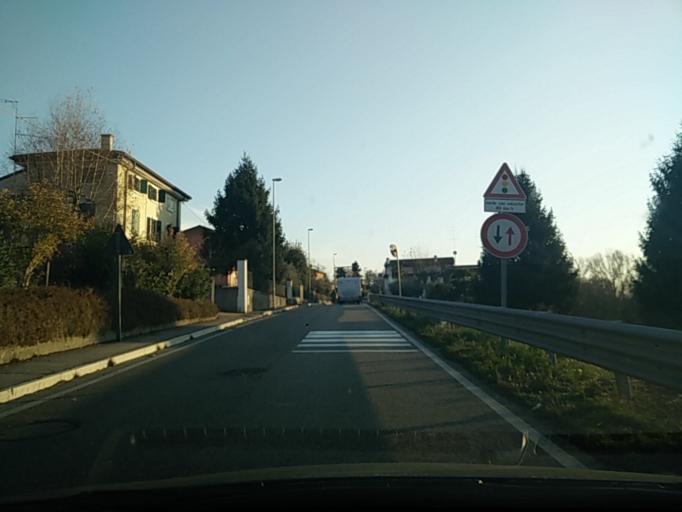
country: IT
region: Veneto
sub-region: Provincia di Verona
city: Salionze
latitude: 45.4086
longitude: 10.7197
